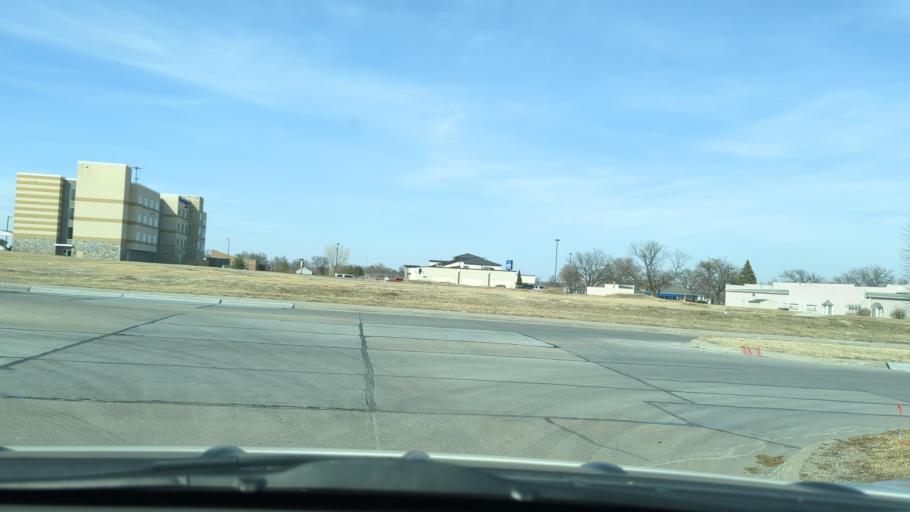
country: US
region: Nebraska
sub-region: Sarpy County
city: Papillion
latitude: 41.1374
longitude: -96.0385
